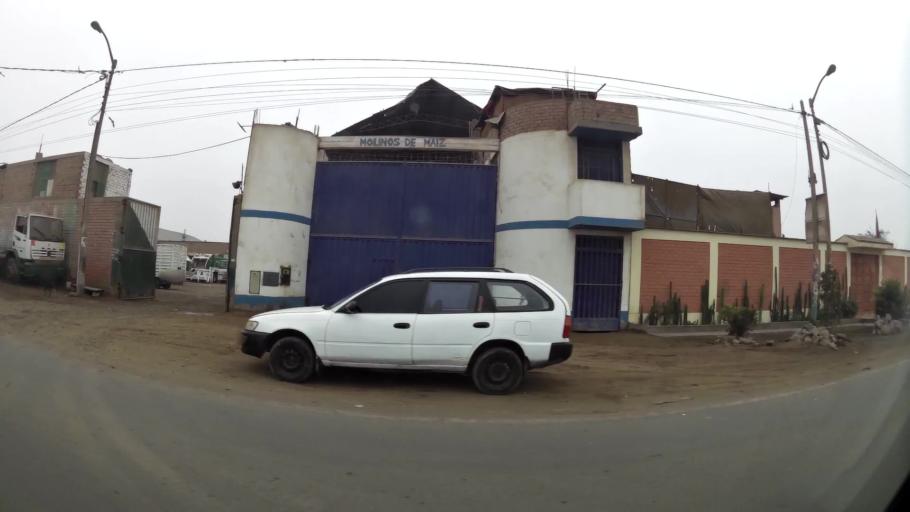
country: PE
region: Lima
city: Ventanilla
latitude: -11.8413
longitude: -77.0991
